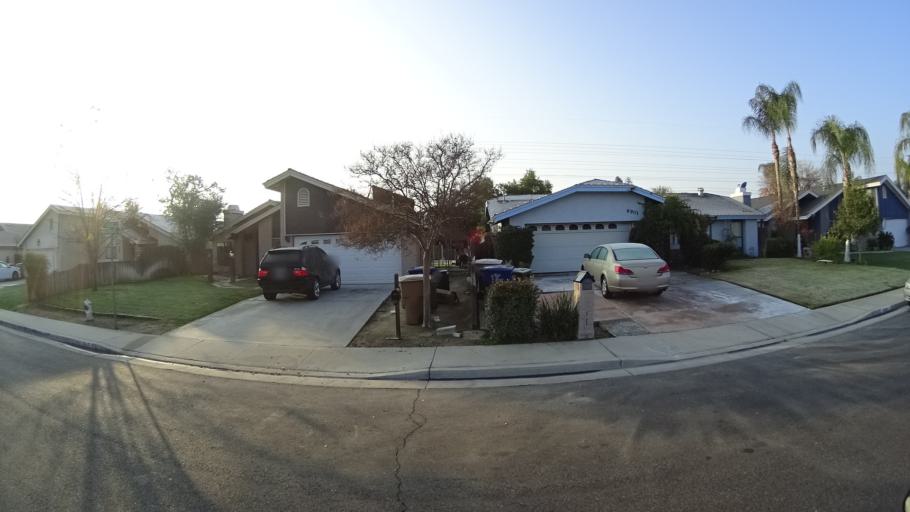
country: US
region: California
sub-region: Kern County
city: Greenacres
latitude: 35.3188
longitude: -119.0808
